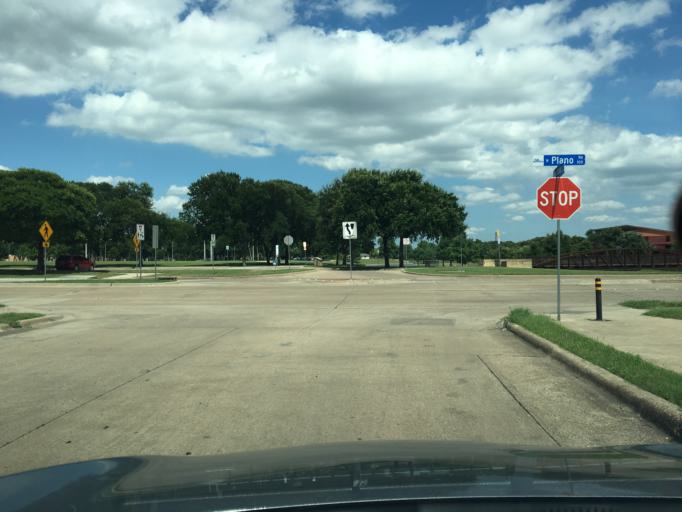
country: US
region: Texas
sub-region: Dallas County
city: Richardson
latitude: 32.9492
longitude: -96.7002
